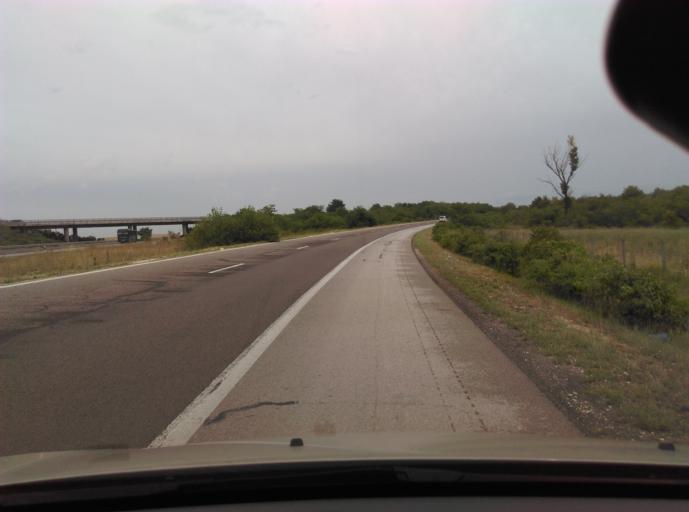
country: BG
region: Stara Zagora
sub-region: Obshtina Chirpan
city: Chirpan
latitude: 42.1935
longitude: 25.2316
